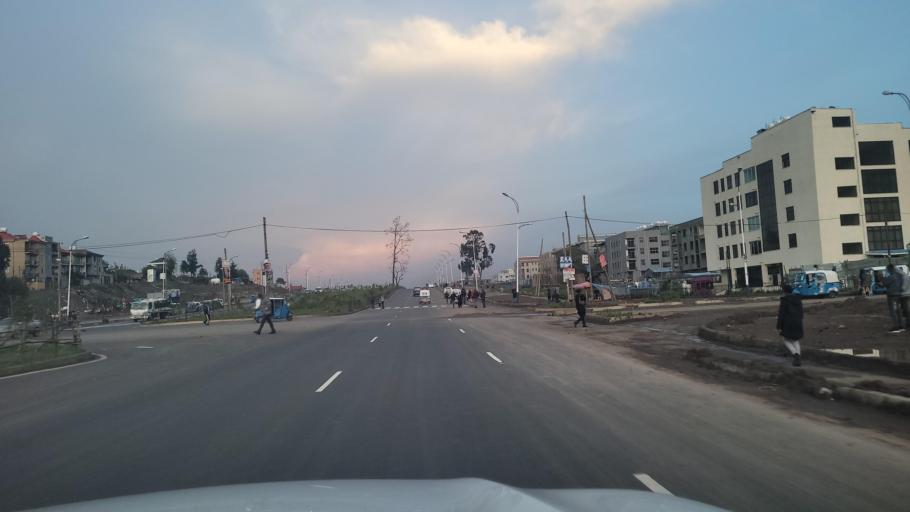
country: ET
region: Adis Abeba
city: Addis Ababa
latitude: 8.9415
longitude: 38.7213
